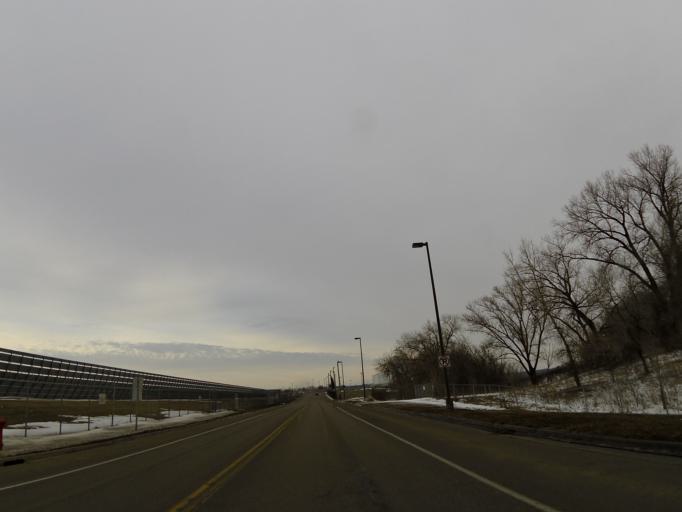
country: US
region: Minnesota
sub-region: Dakota County
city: Mendota Heights
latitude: 44.8732
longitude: -93.2067
